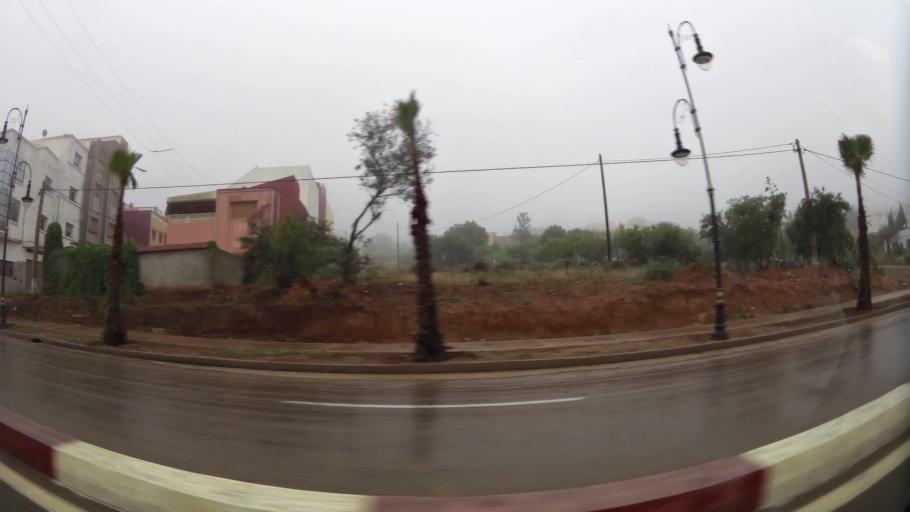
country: MA
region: Taza-Al Hoceima-Taounate
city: Tirhanimine
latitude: 35.1965
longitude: -3.9195
